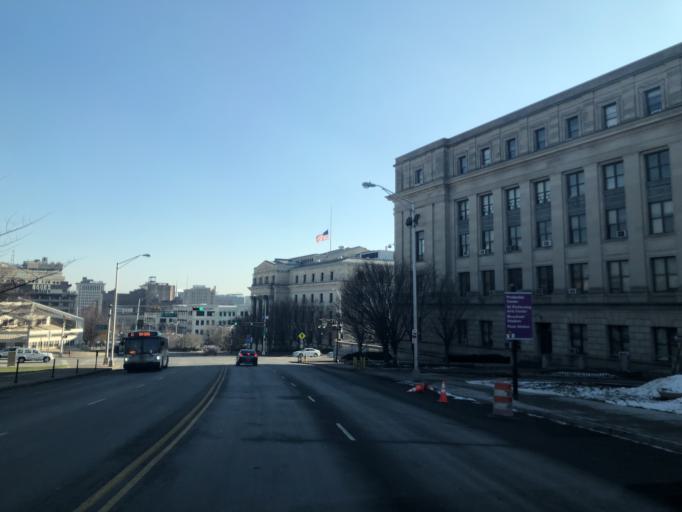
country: US
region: New Jersey
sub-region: Essex County
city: Newark
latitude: 40.7383
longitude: -74.1800
